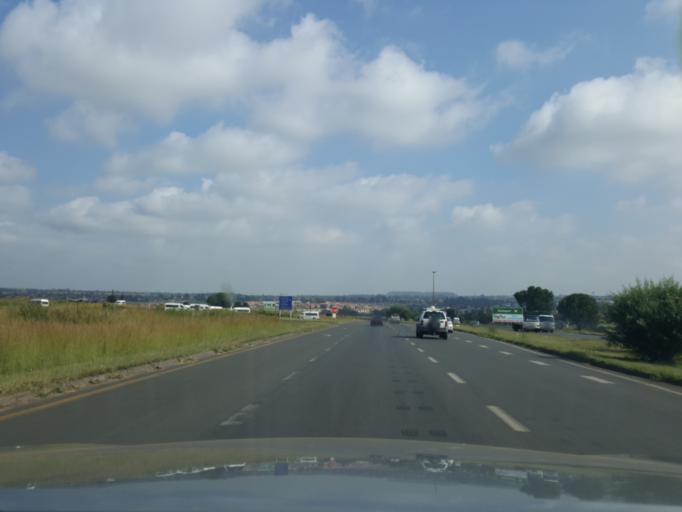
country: ZA
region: Mpumalanga
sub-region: Nkangala District Municipality
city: Witbank
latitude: -25.9415
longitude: 29.2421
